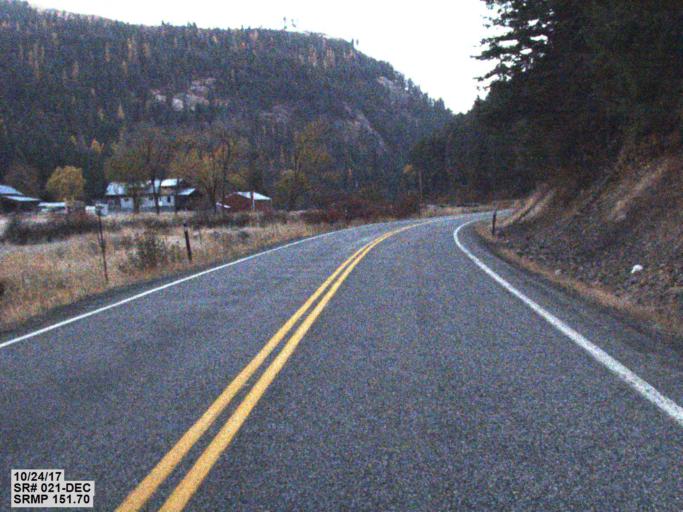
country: US
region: Washington
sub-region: Ferry County
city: Republic
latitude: 48.5285
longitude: -118.7340
